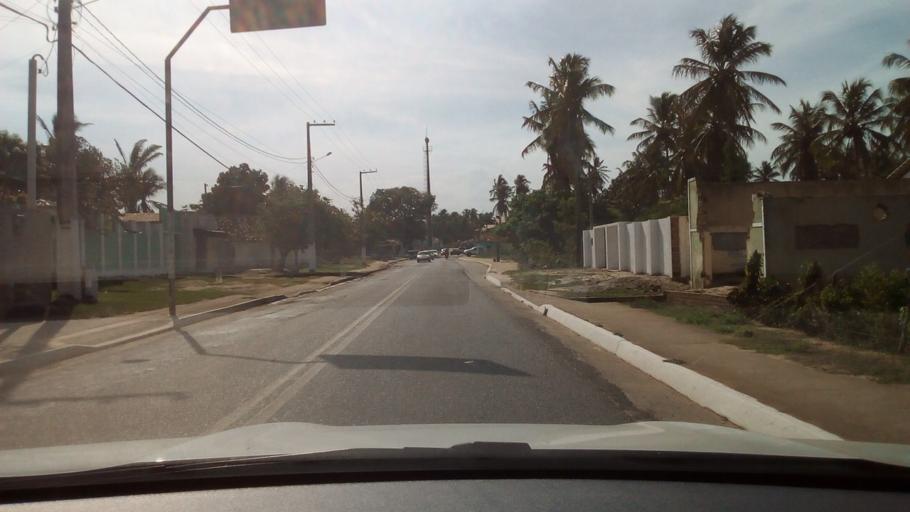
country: BR
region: Rio Grande do Norte
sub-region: Ares
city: Ares
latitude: -6.2339
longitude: -35.1508
